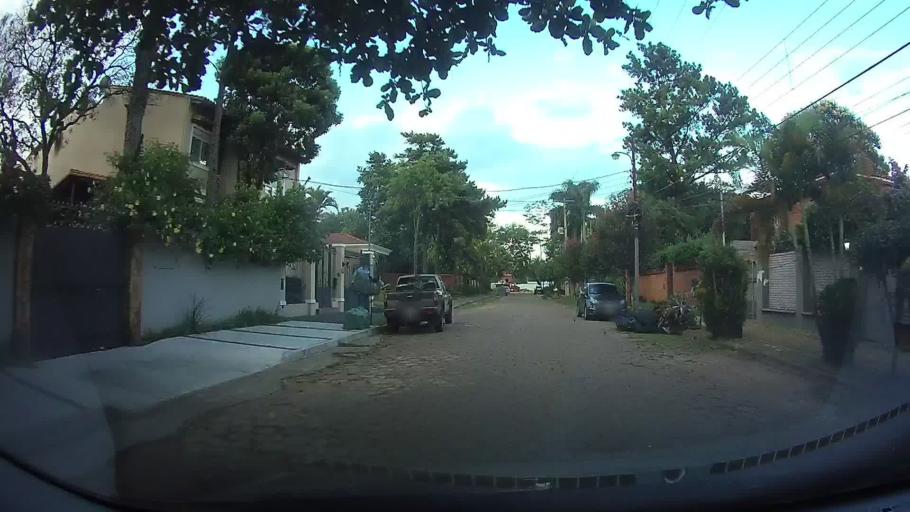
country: PY
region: Central
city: Fernando de la Mora
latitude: -25.2743
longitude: -57.5607
